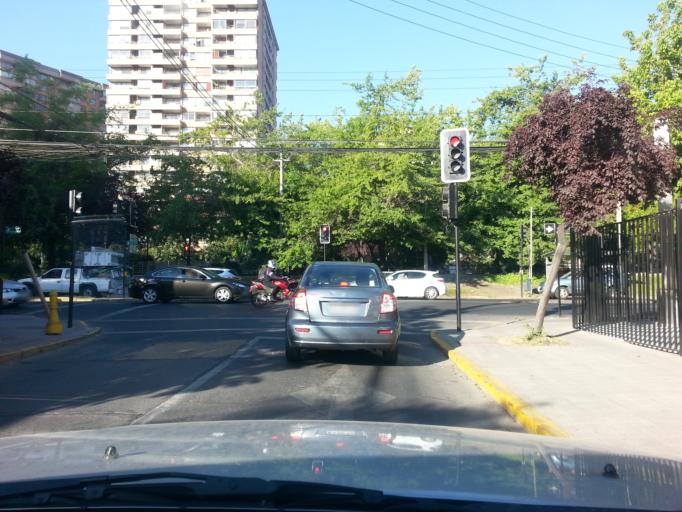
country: CL
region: Santiago Metropolitan
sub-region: Provincia de Santiago
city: Villa Presidente Frei, Nunoa, Santiago, Chile
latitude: -33.4282
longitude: -70.5891
